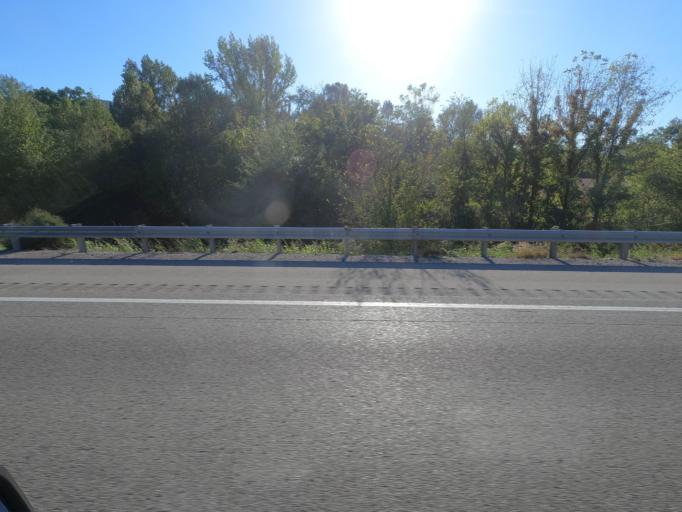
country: US
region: Tennessee
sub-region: Marion County
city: South Pittsburg
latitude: 35.0604
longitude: -85.7238
